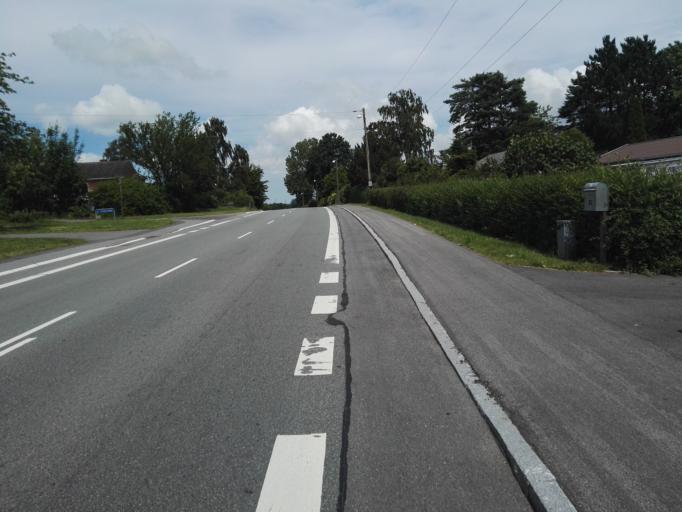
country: DK
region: Capital Region
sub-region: Frederikssund Kommune
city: Slangerup
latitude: 55.8547
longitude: 12.1733
